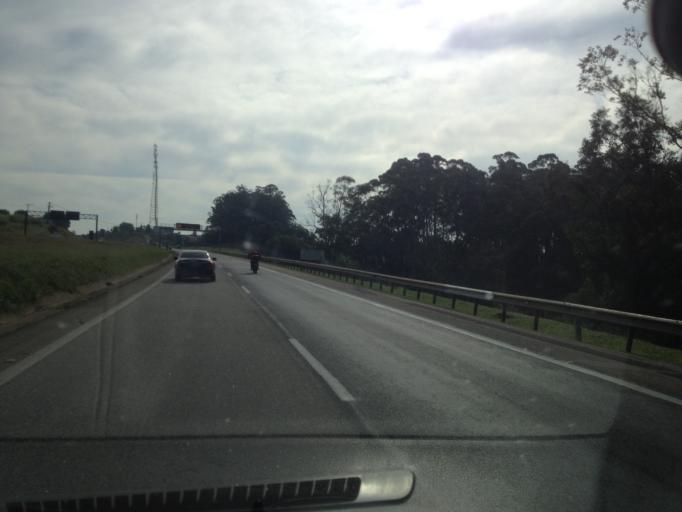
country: BR
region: Sao Paulo
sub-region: Itu
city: Itu
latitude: -23.3866
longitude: -47.3290
